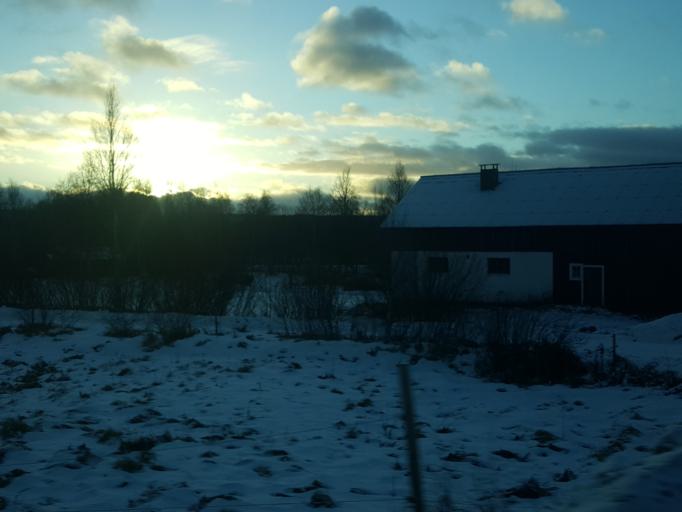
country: SE
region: Jaemtland
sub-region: Harjedalens Kommun
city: Sveg
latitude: 62.4439
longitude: 13.8736
